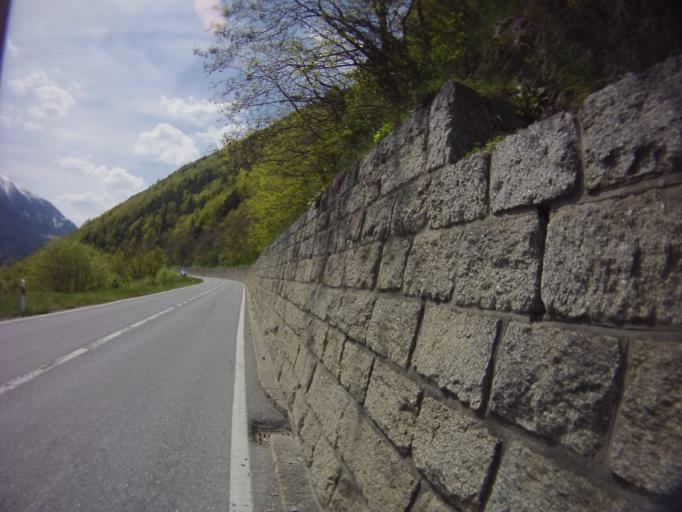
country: CH
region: Valais
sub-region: Martigny District
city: Martigny-Combe
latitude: 46.0918
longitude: 7.0485
